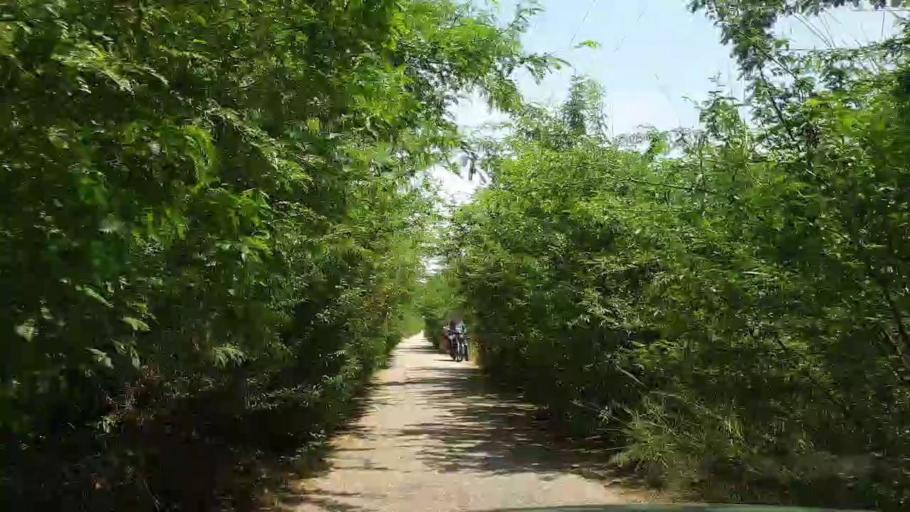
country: PK
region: Sindh
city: Kot Diji
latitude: 27.1337
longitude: 69.0056
